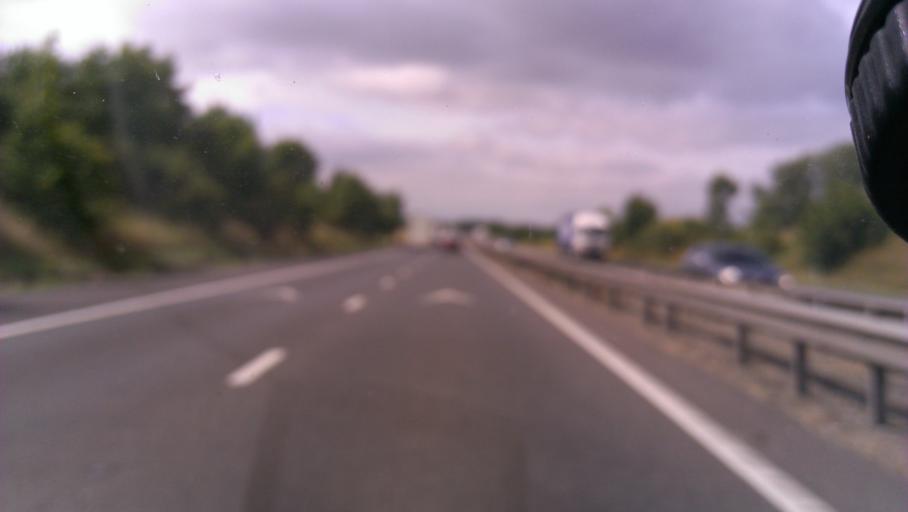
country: GB
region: England
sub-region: Cambridgeshire
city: Harston
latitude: 52.1299
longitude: 0.1179
